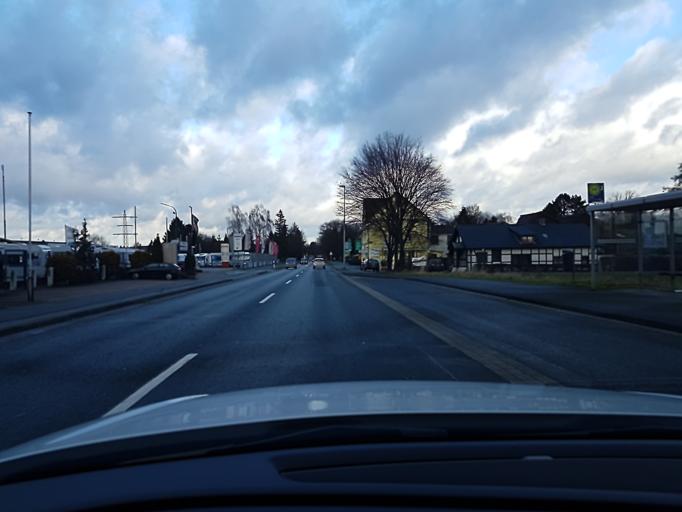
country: DE
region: North Rhine-Westphalia
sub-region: Regierungsbezirk Dusseldorf
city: Muelheim (Ruhr)
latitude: 51.3819
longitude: 6.8644
